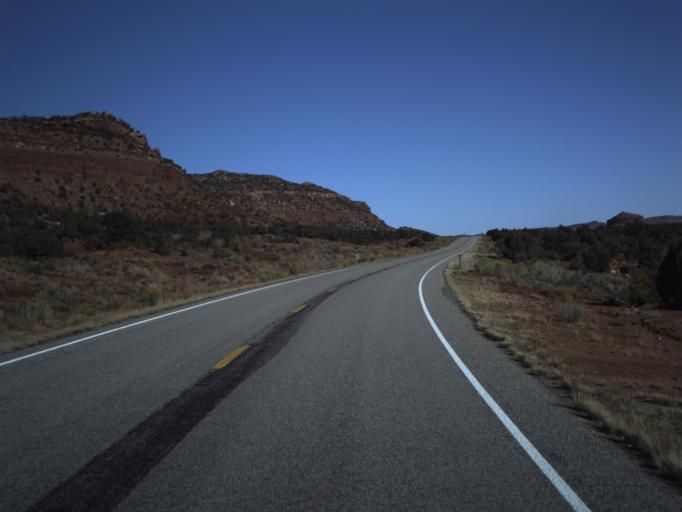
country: US
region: Utah
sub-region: San Juan County
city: Blanding
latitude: 37.6048
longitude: -110.0787
